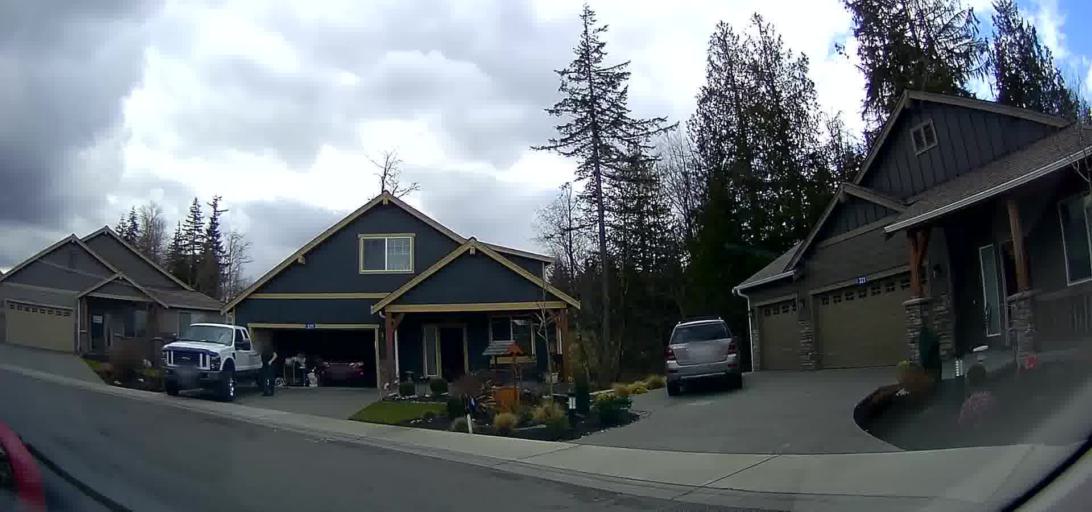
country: US
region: Washington
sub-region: Skagit County
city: Big Lake
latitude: 48.4232
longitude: -122.2817
